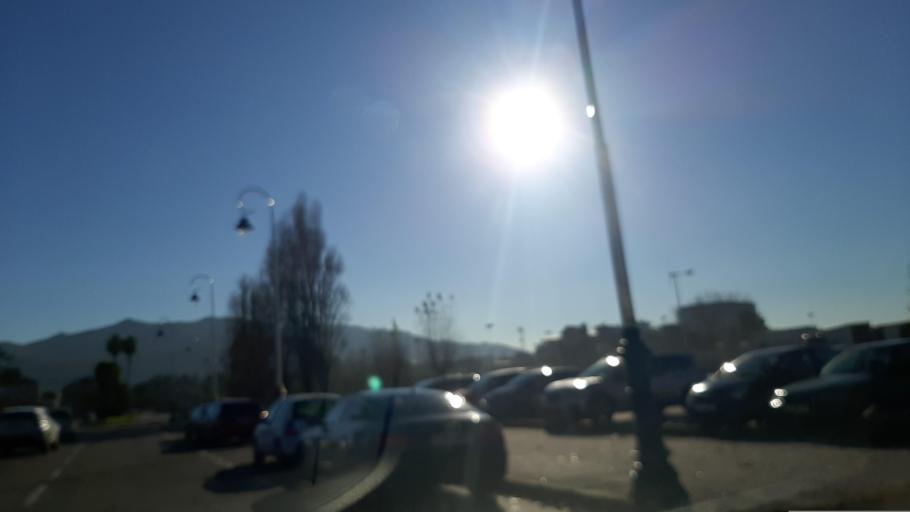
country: ES
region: Galicia
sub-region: Provincia de Pontevedra
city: Cangas
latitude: 42.2055
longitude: -8.7770
